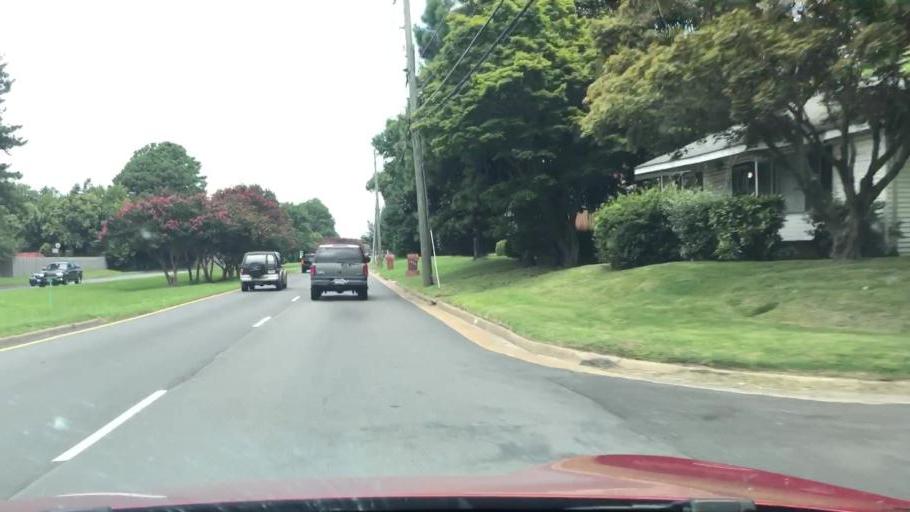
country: US
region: Virginia
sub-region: City of Norfolk
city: Norfolk
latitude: 36.8880
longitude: -76.1368
